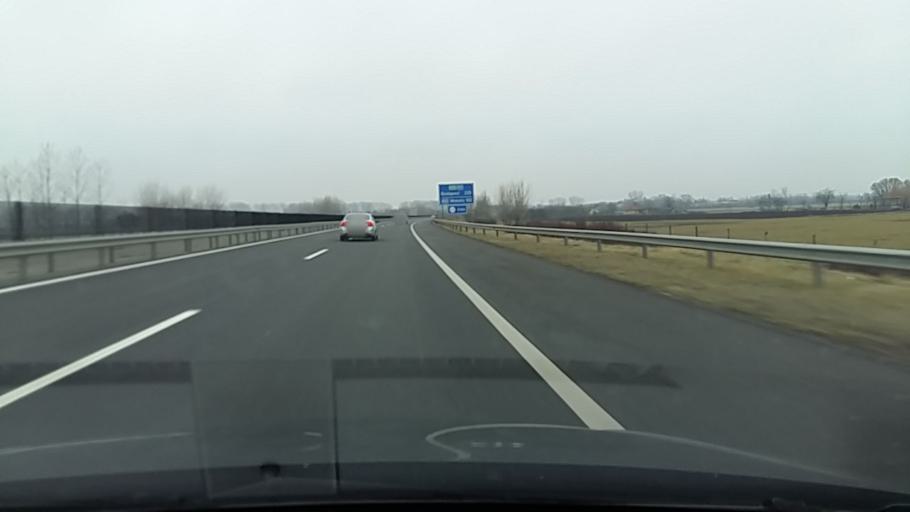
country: HU
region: Szabolcs-Szatmar-Bereg
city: Nyiregyhaza
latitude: 47.8862
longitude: 21.6996
